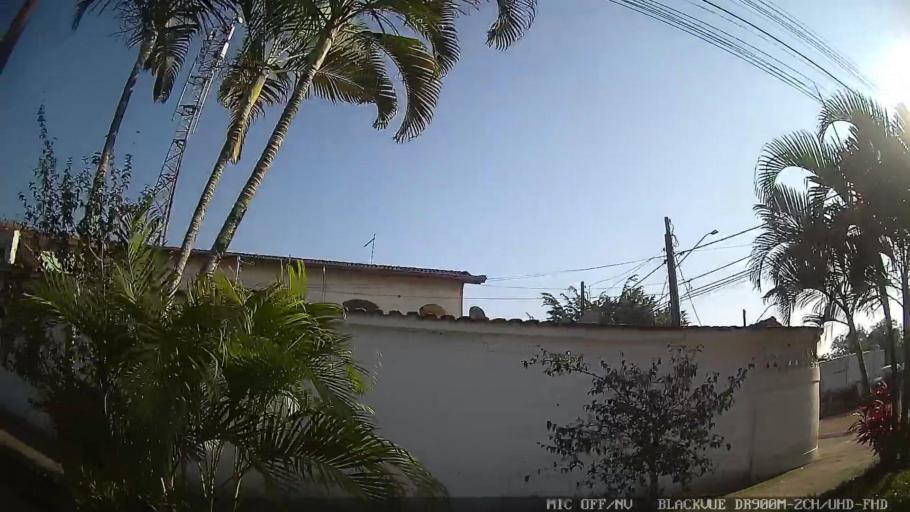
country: BR
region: Sao Paulo
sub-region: Guaruja
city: Guaruja
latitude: -23.9835
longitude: -46.2701
